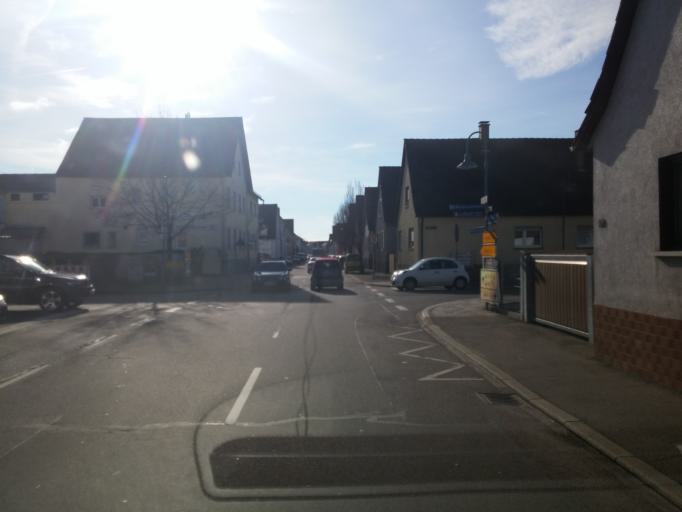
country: DE
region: Baden-Wuerttemberg
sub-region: Karlsruhe Region
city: Karlsdorf-Neuthard
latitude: 49.1305
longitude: 8.5220
